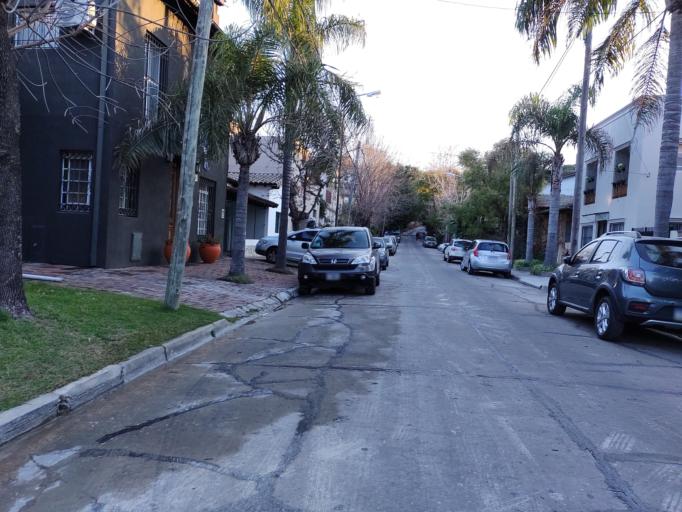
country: AR
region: Buenos Aires
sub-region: Partido de San Isidro
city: San Isidro
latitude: -34.4459
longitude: -58.5341
